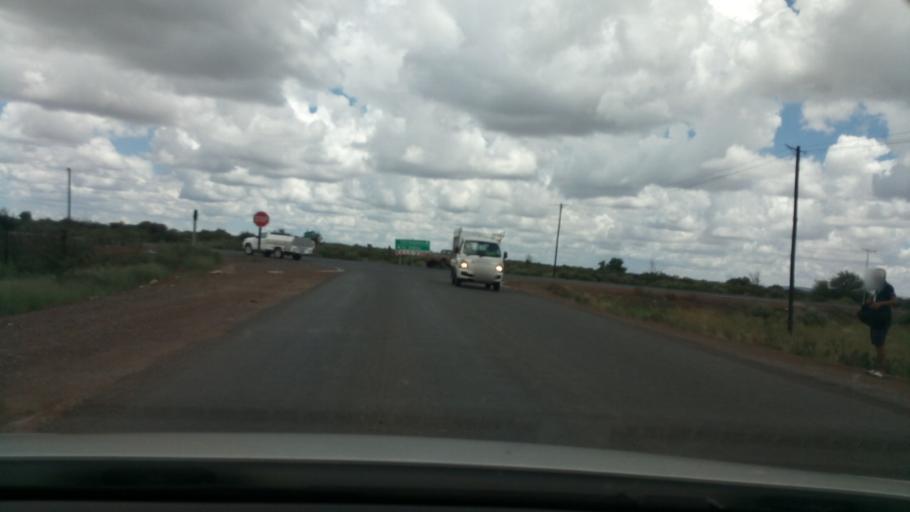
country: ZA
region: Northern Cape
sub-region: Siyanda District Municipality
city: Danielskuil
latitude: -28.2620
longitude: 23.5596
